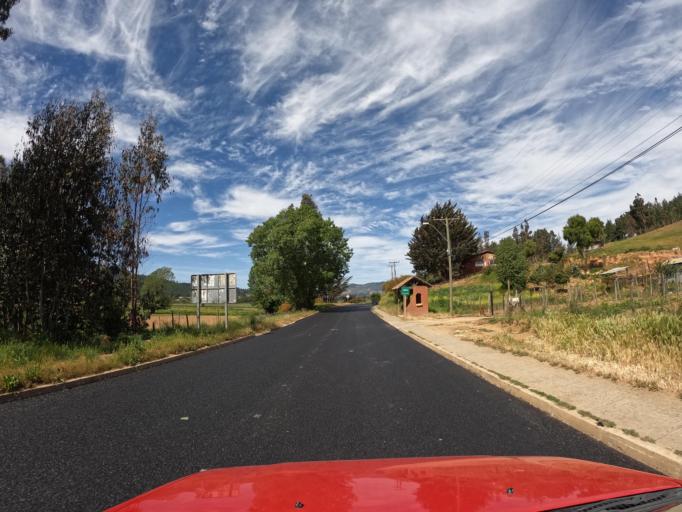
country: CL
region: Maule
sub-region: Provincia de Talca
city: Constitucion
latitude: -35.0977
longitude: -72.0078
